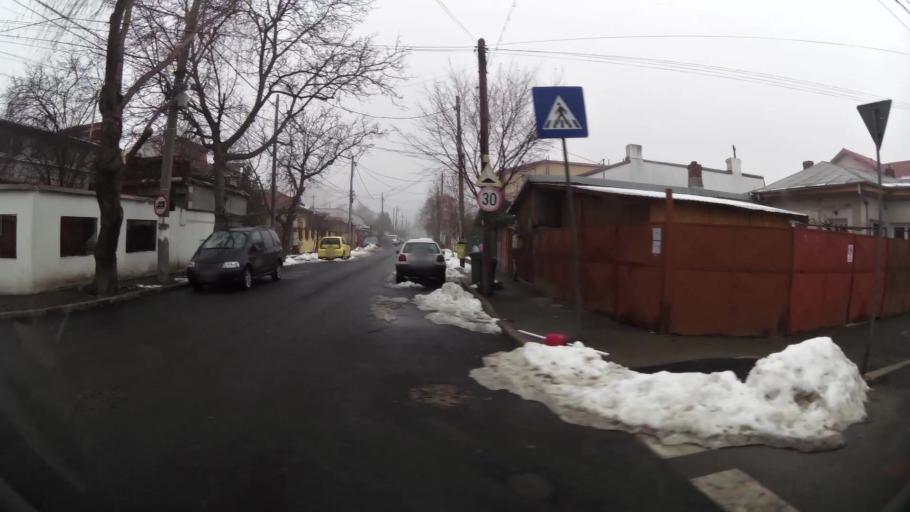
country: RO
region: Ilfov
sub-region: Comuna Chiajna
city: Rosu
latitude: 44.4749
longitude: 26.0429
